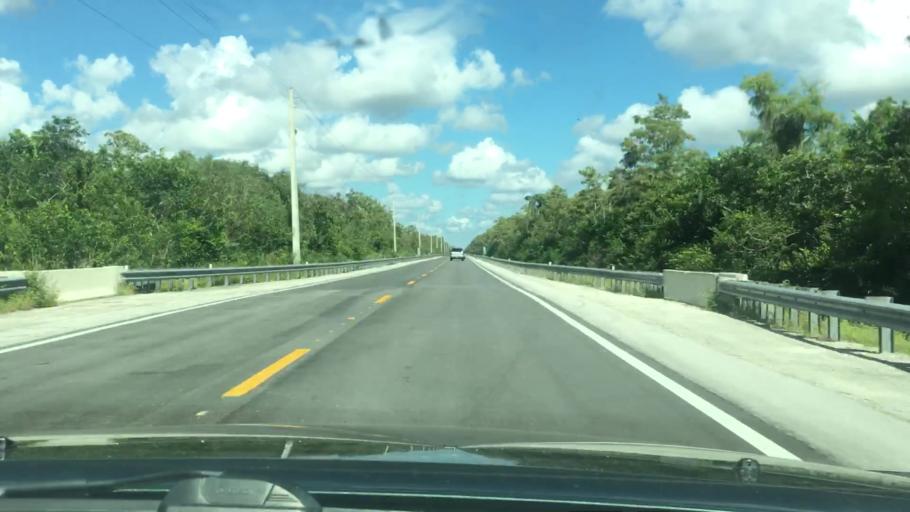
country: US
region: Florida
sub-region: Miami-Dade County
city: Kendall West
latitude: 25.7694
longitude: -80.8360
